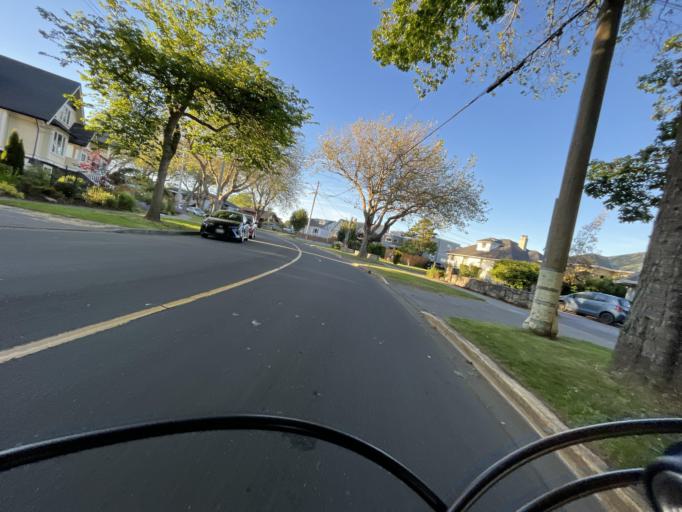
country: CA
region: British Columbia
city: Victoria
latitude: 48.4091
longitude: -123.3308
